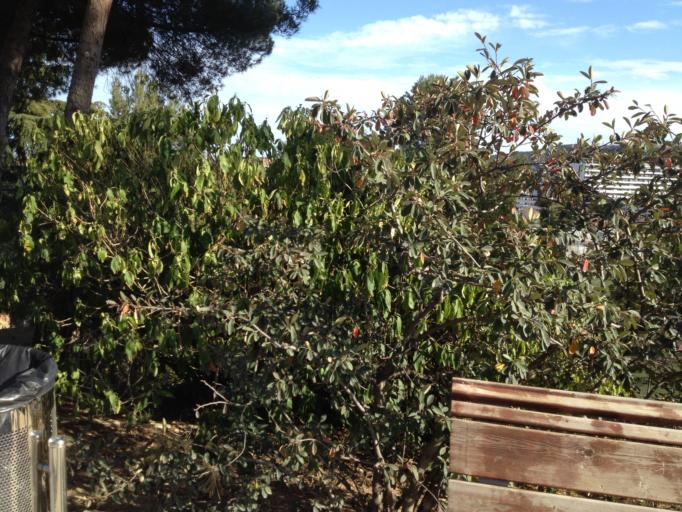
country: ES
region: Catalonia
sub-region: Provincia de Barcelona
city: Horta-Guinardo
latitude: 41.4371
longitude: 2.1470
